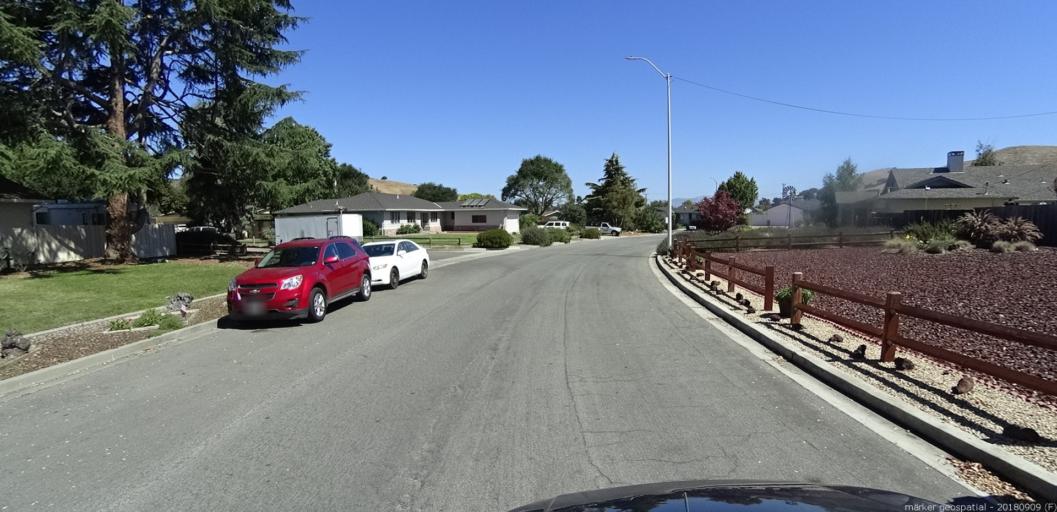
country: US
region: California
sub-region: Monterey County
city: Salinas
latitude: 36.6099
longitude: -121.6945
